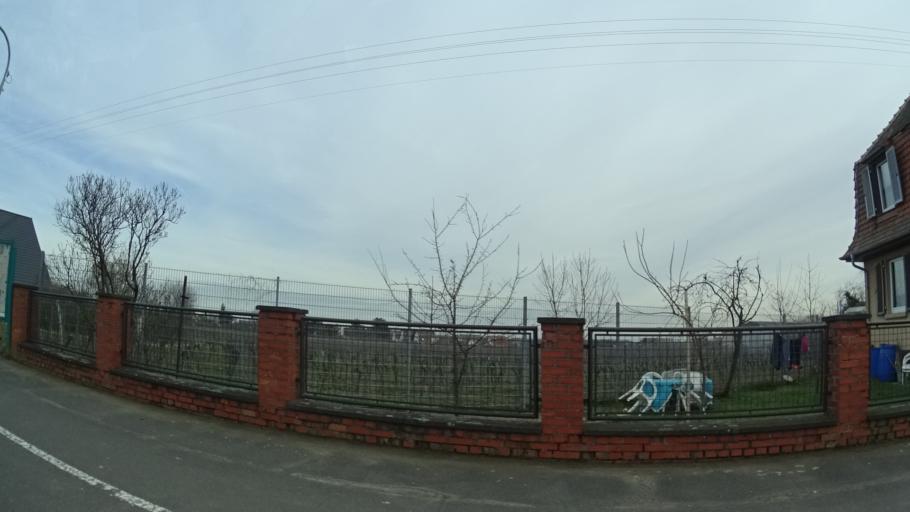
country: DE
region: Rheinland-Pfalz
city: Neustadt
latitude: 49.3669
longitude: 8.1654
